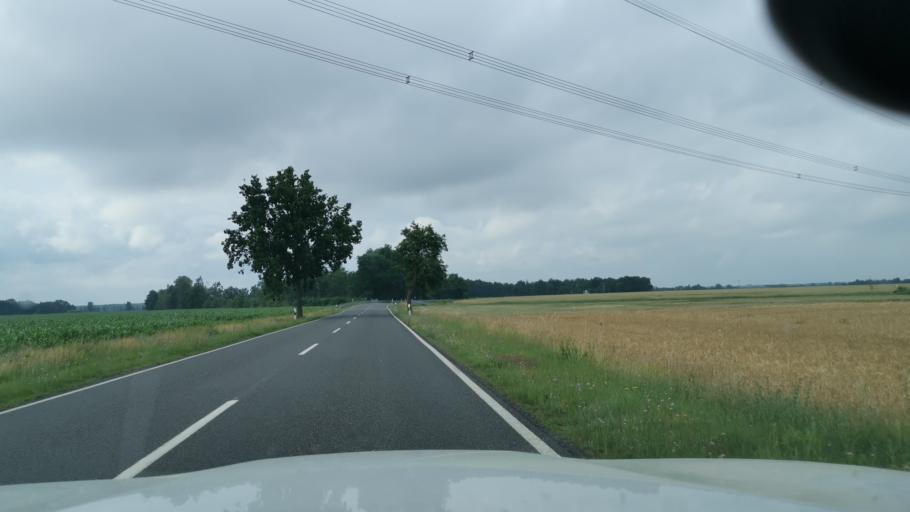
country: DE
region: Saxony-Anhalt
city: Annaburg
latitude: 51.7794
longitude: 13.0296
